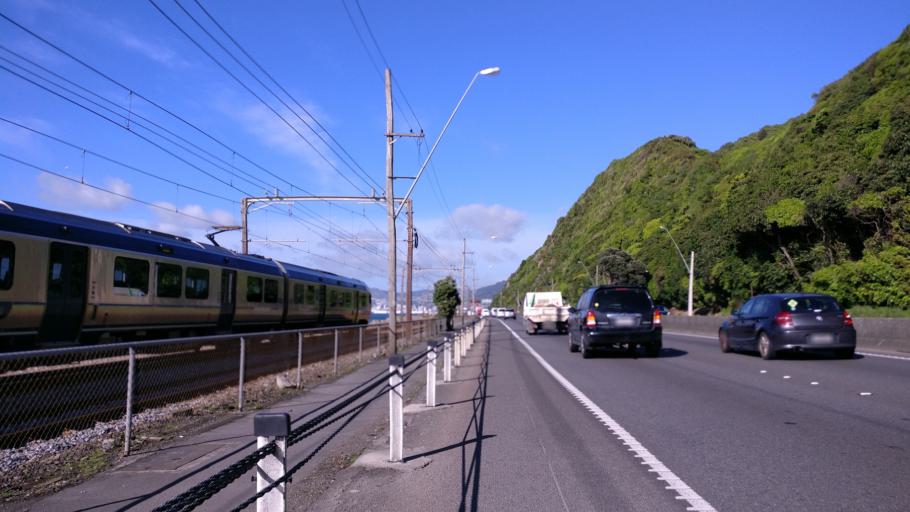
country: NZ
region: Wellington
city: Petone
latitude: -41.2381
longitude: 174.8293
